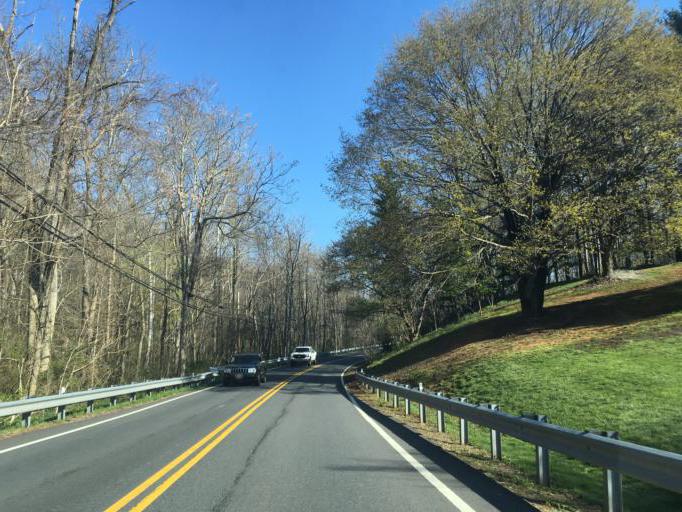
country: US
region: Maryland
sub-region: Frederick County
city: Myersville
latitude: 39.5179
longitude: -77.5479
